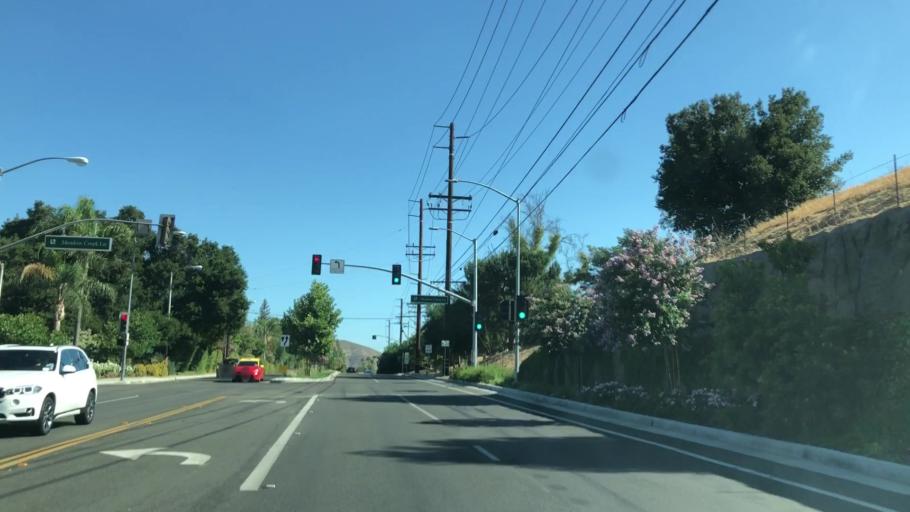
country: US
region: California
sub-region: Los Angeles County
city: Agoura
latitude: 34.1300
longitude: -118.7036
